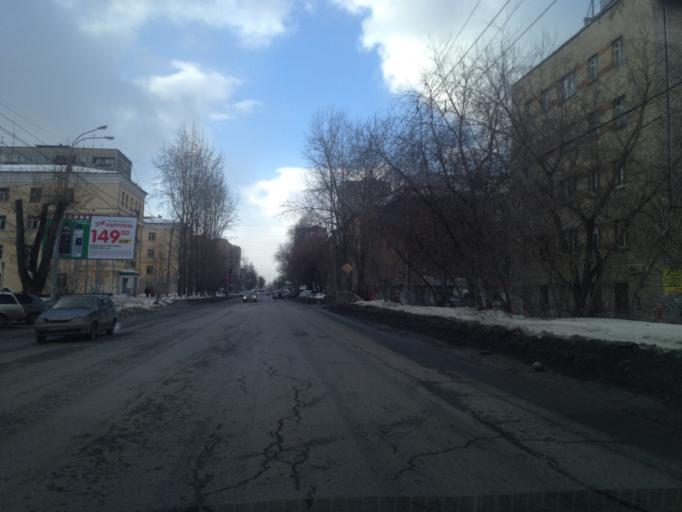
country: RU
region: Sverdlovsk
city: Yekaterinburg
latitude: 56.8615
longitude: 60.6433
